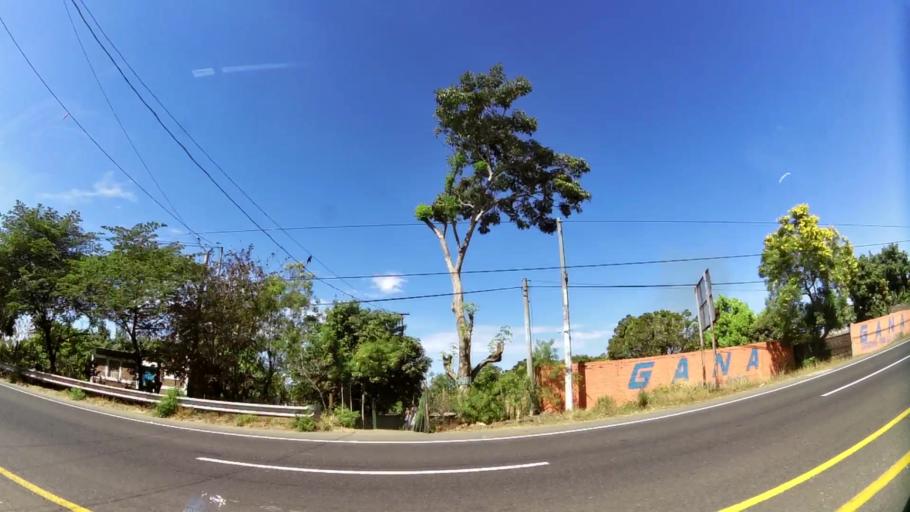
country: SV
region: Ahuachapan
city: Atiquizaya
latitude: 13.9706
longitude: -89.7523
